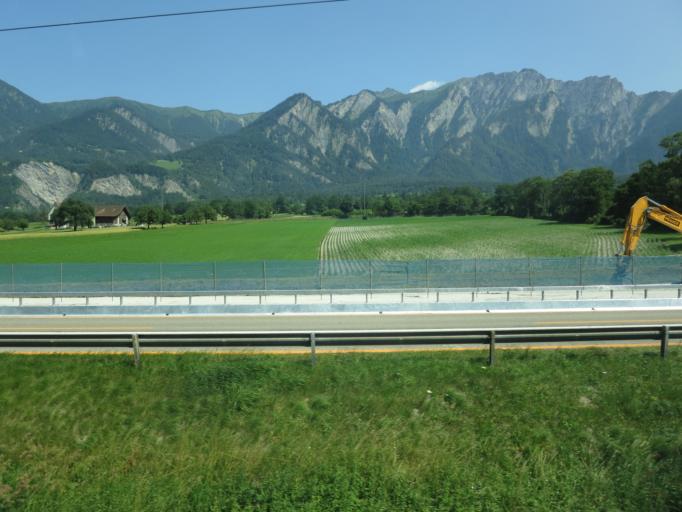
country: CH
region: Grisons
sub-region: Landquart District
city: Trimmis
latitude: 46.8954
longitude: 9.5419
